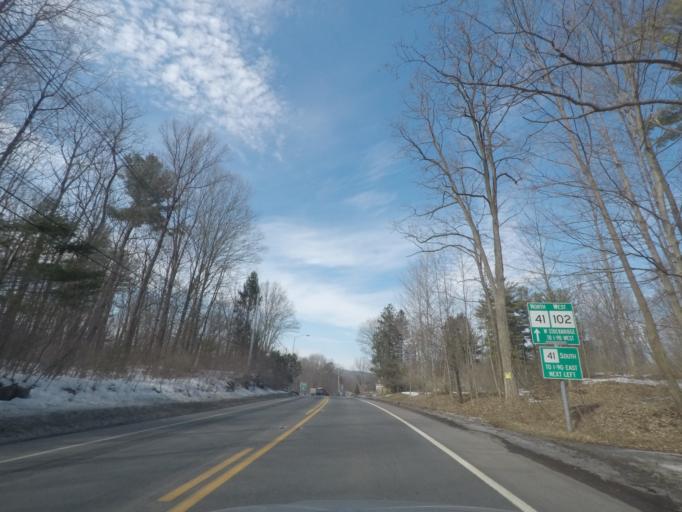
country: US
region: Massachusetts
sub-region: Berkshire County
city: West Stockbridge
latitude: 42.3293
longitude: -73.3639
